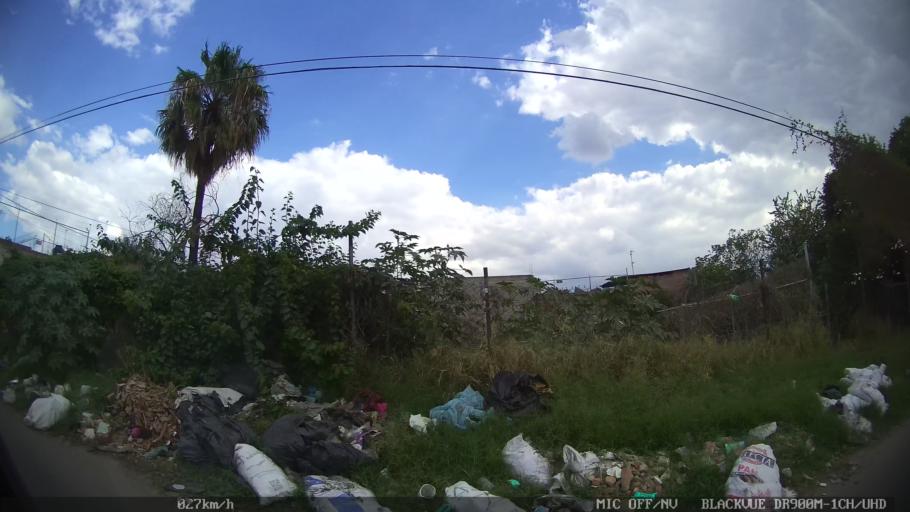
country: MX
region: Jalisco
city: Tlaquepaque
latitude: 20.6566
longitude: -103.2670
